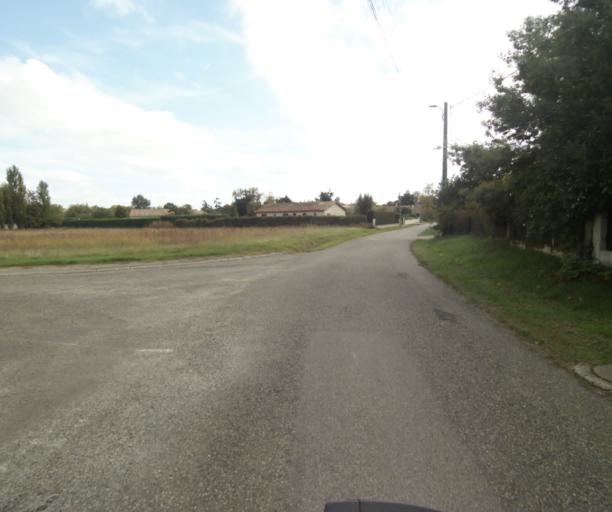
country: FR
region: Midi-Pyrenees
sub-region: Departement du Tarn-et-Garonne
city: Finhan
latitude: 43.9206
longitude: 1.2178
